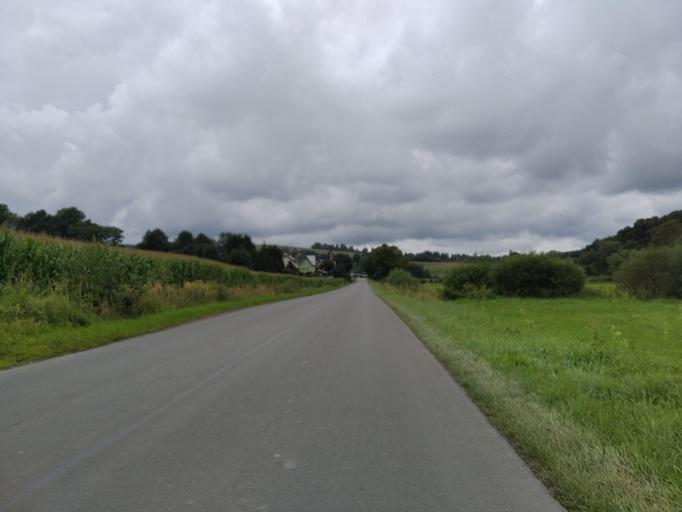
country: PL
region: Subcarpathian Voivodeship
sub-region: Powiat przemyski
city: Bircza
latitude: 49.7003
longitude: 22.3737
